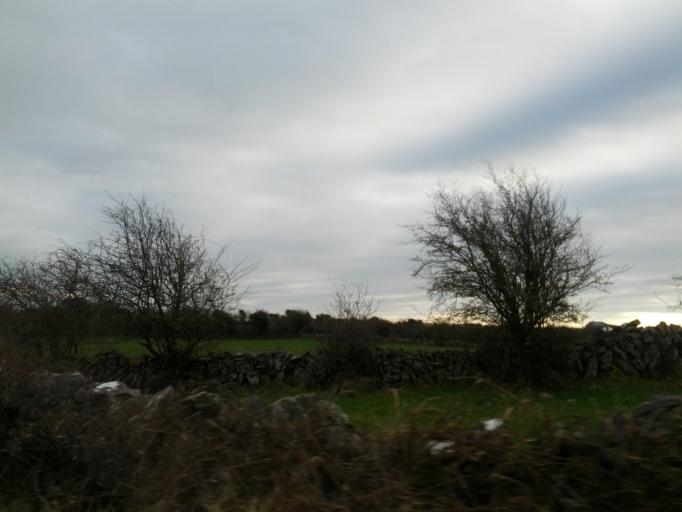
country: IE
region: Connaught
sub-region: County Galway
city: Gort
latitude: 53.1545
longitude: -8.8627
